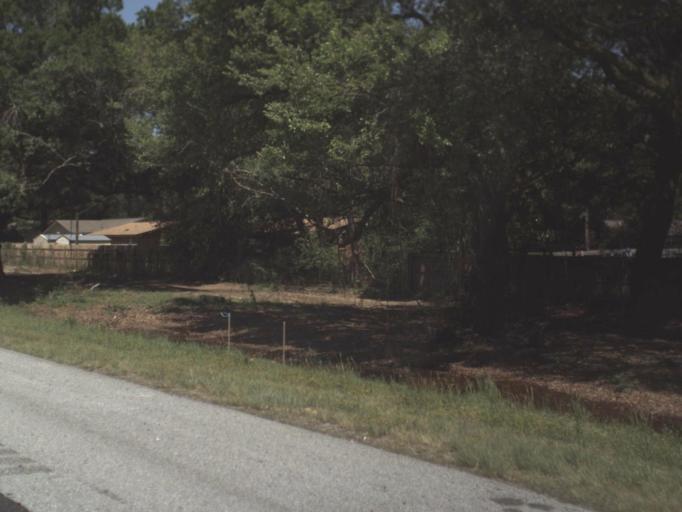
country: US
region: Florida
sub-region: Escambia County
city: Ferry Pass
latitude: 30.5027
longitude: -87.1897
